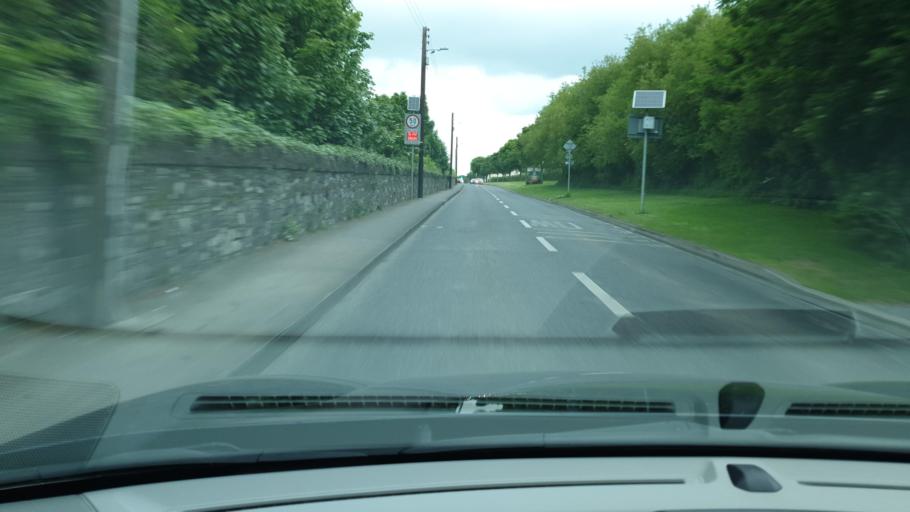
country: IE
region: Leinster
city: Balbriggan
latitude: 53.6036
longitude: -6.1686
